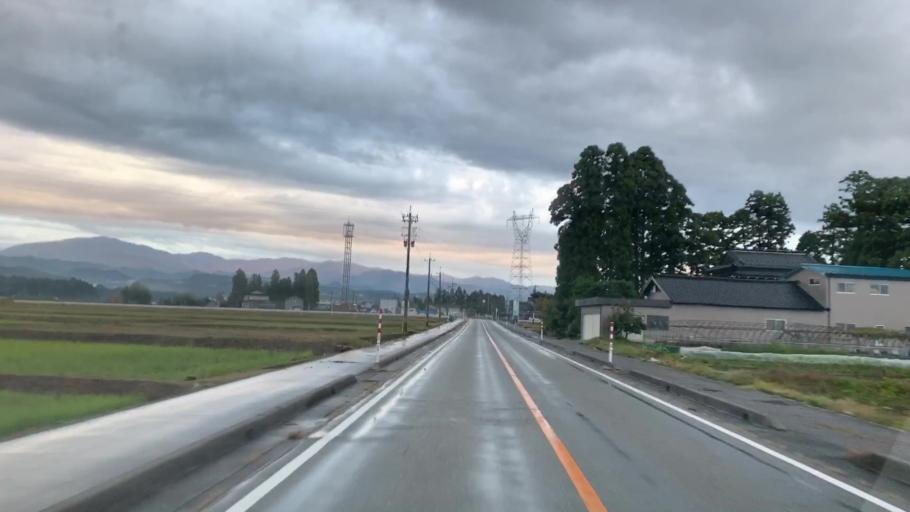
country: JP
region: Toyama
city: Kamiichi
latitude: 36.6603
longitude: 137.3273
